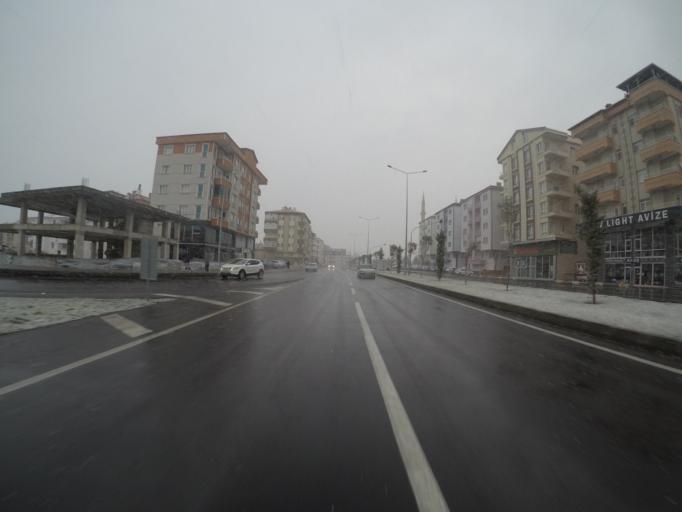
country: TR
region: Nevsehir
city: Nevsehir
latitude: 38.6319
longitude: 34.7294
